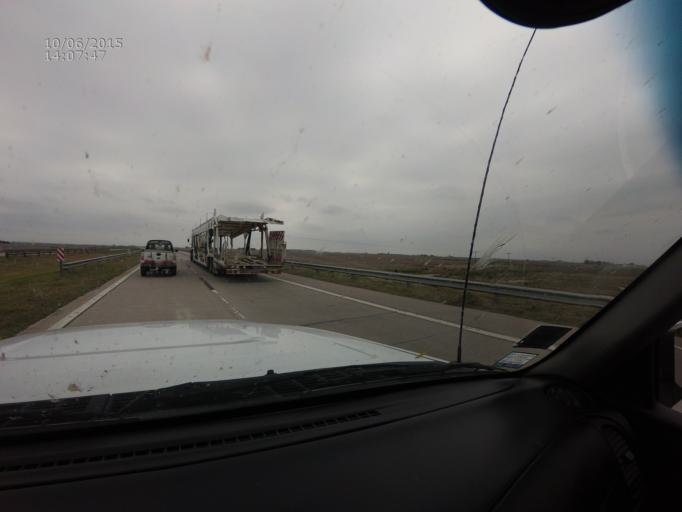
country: AR
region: Cordoba
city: Villa Nueva
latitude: -32.4836
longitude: -63.0332
